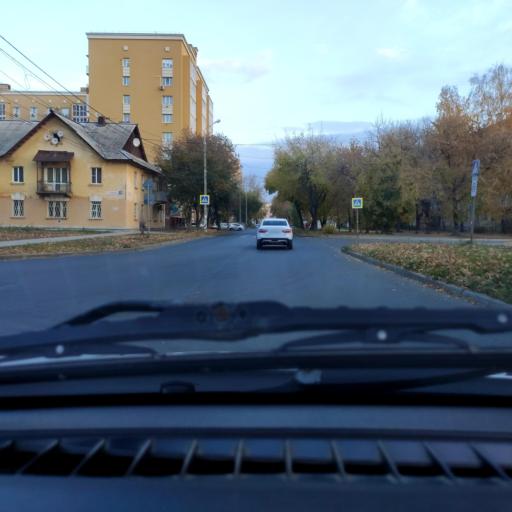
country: RU
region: Samara
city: Tol'yatti
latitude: 53.5008
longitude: 49.3964
